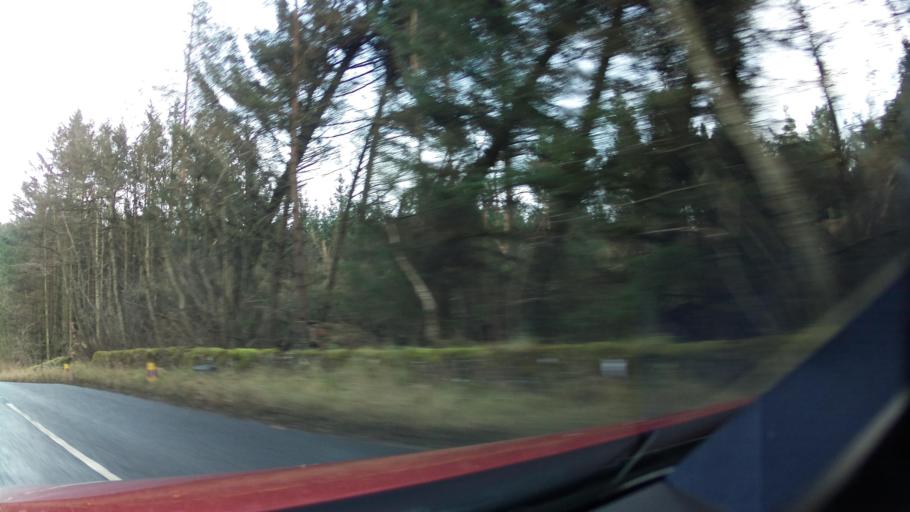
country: GB
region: Scotland
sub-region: Angus
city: Letham
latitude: 56.5474
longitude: -2.7699
